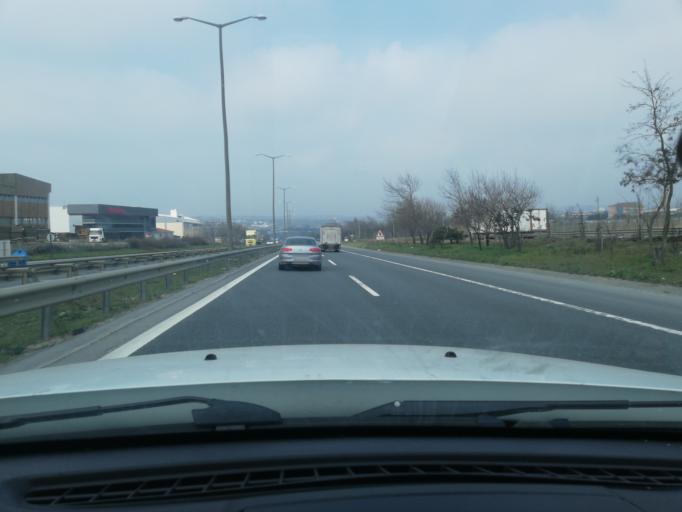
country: TR
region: Istanbul
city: Ortakoy
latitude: 41.0854
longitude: 28.3682
